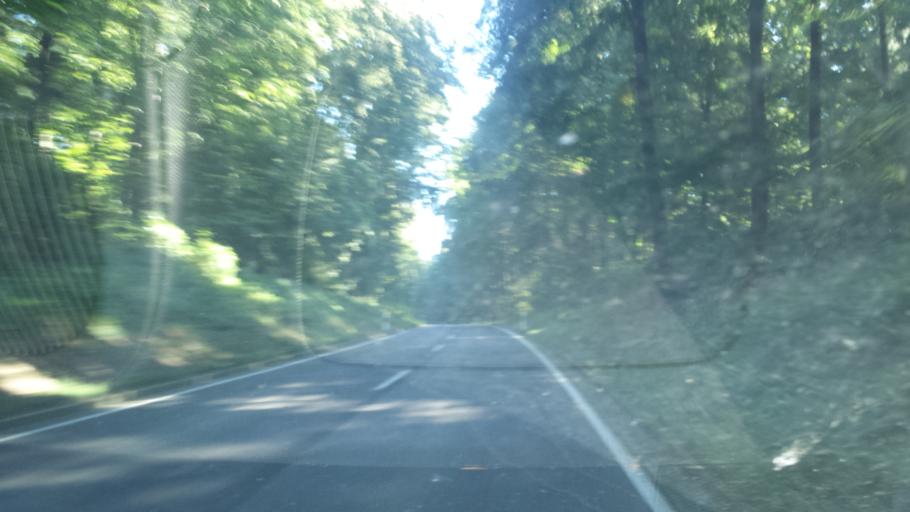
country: DE
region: Bavaria
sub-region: Lower Bavaria
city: Kelheim
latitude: 48.9001
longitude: 11.8569
